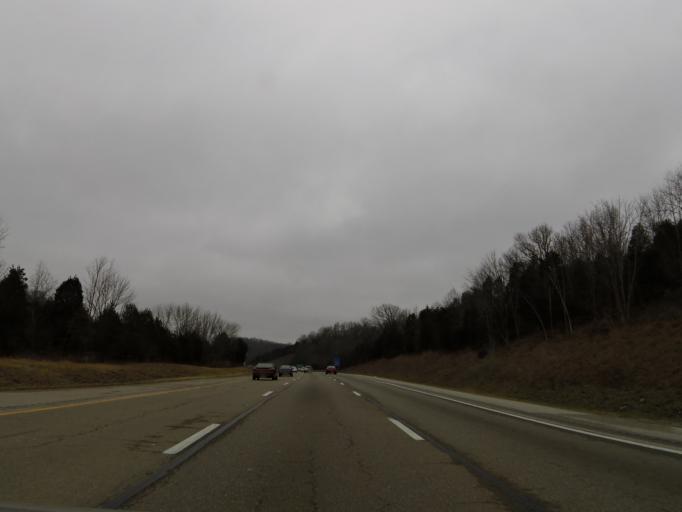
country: US
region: Kentucky
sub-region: Grant County
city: Williamstown
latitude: 38.4762
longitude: -84.5811
